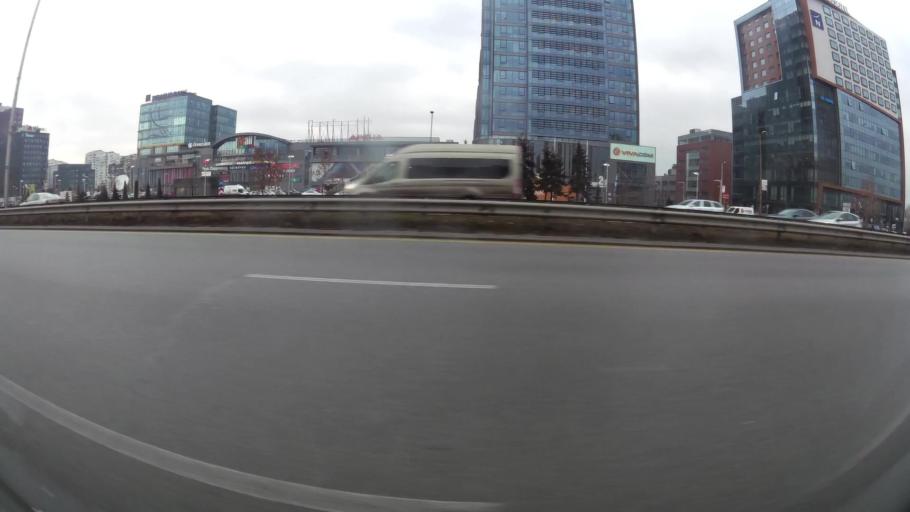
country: BG
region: Sofia-Capital
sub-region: Stolichna Obshtina
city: Sofia
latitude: 42.6591
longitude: 23.3816
